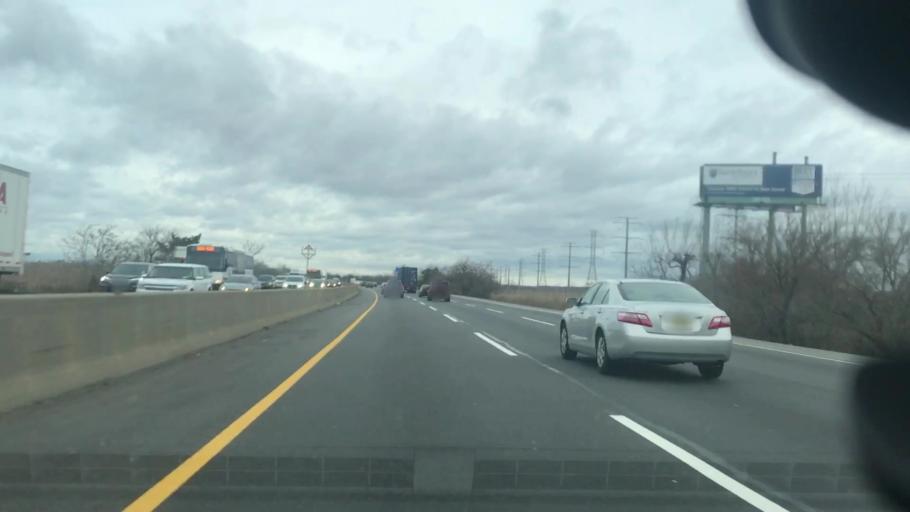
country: US
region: New Jersey
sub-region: Hudson County
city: North Bergen
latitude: 40.8095
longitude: -74.0302
